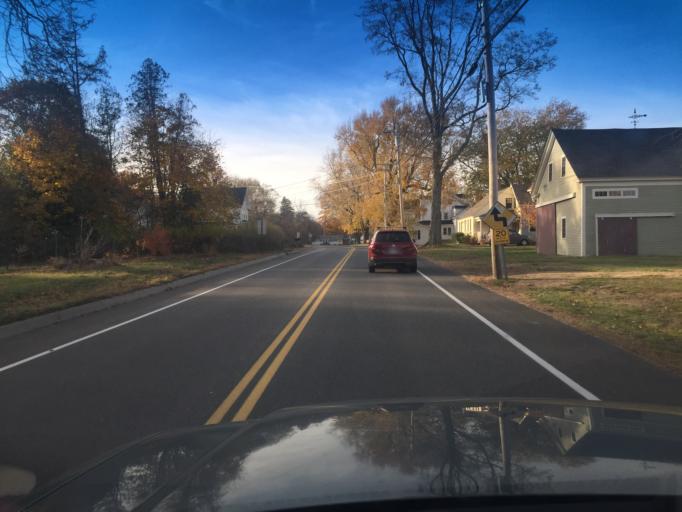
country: US
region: Maine
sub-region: York County
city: York Harbor
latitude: 43.1551
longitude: -70.6869
